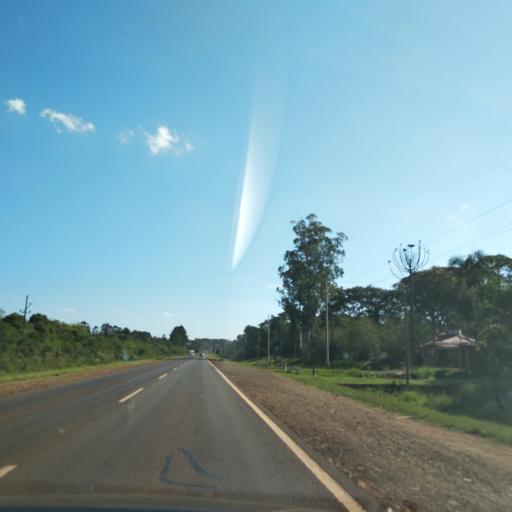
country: AR
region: Misiones
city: Jardin America
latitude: -27.0258
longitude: -55.2095
